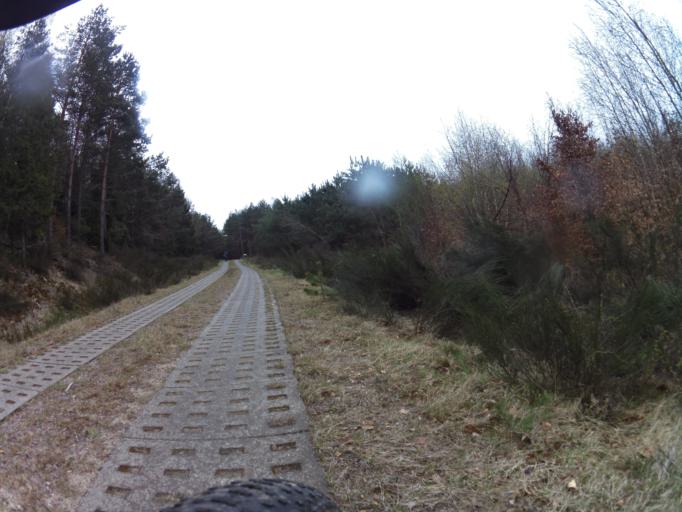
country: PL
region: West Pomeranian Voivodeship
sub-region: Powiat koszalinski
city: Polanow
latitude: 54.0620
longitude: 16.6265
